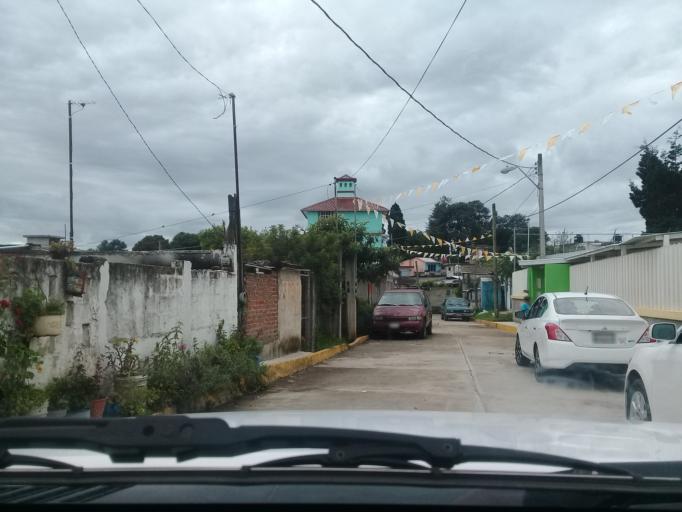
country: MX
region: Veracruz
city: Rafael Lucio
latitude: 19.5976
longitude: -96.9884
